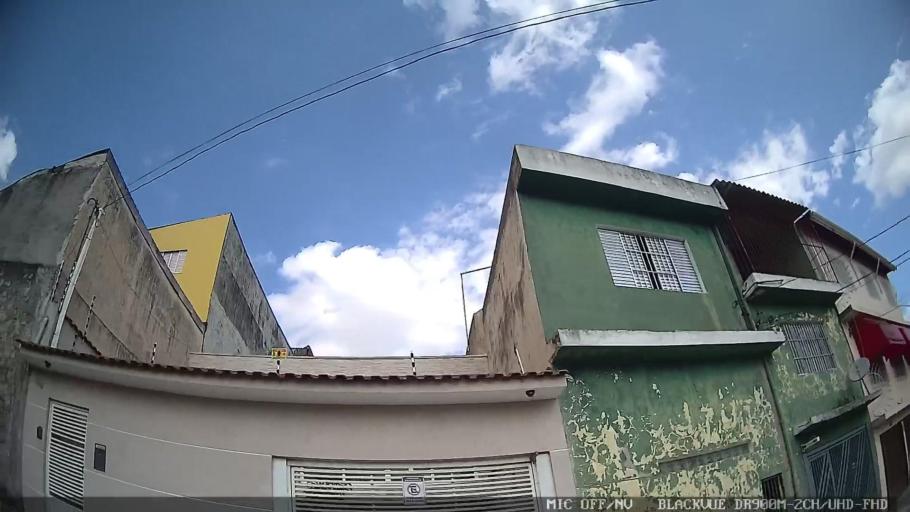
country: BR
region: Sao Paulo
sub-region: Guarulhos
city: Guarulhos
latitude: -23.4905
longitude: -46.4774
